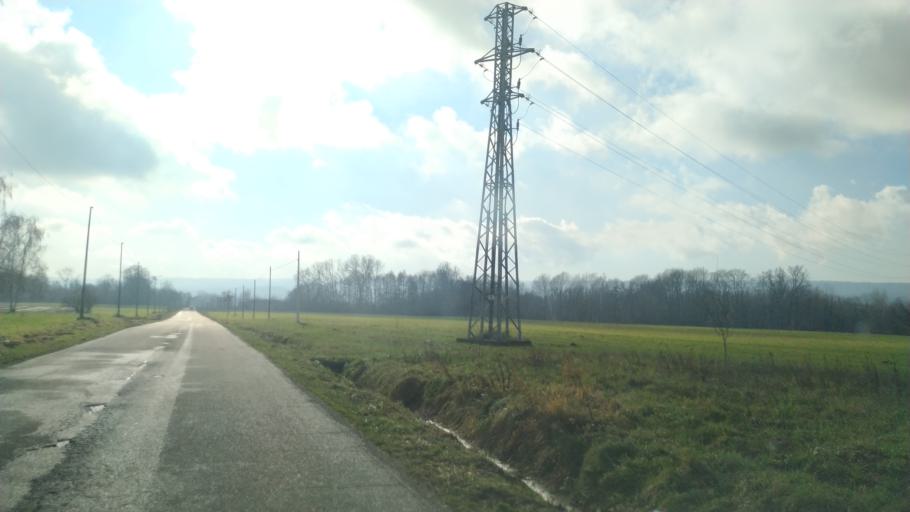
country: IT
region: Piedmont
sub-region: Provincia di Biella
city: Occhieppo Inferiore
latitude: 45.5423
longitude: 8.0252
